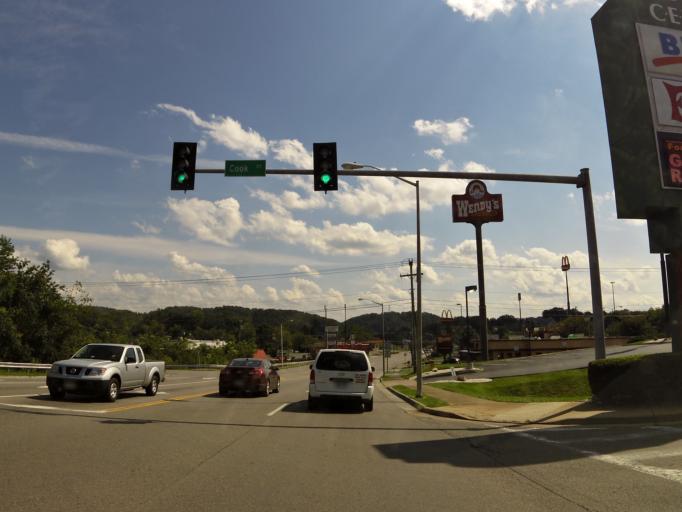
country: US
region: Virginia
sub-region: Washington County
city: Abingdon
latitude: 36.7029
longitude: -81.9743
